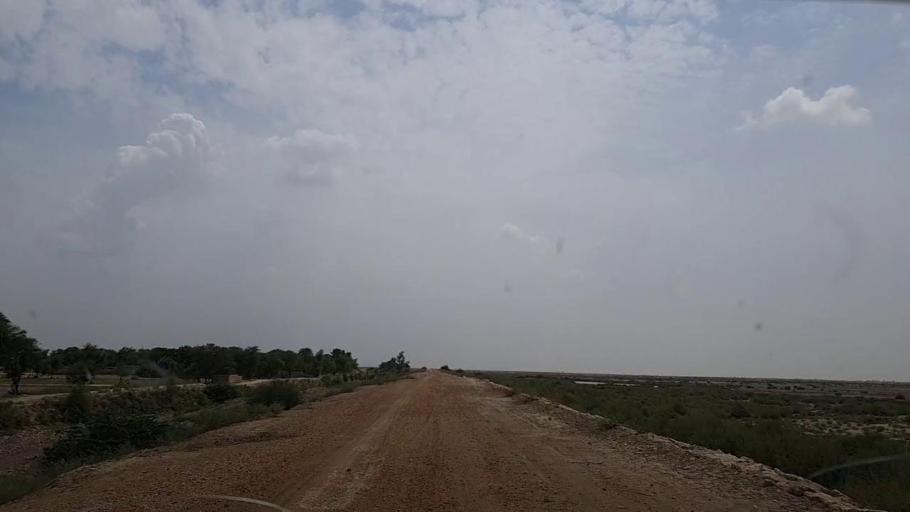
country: PK
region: Sindh
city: Phulji
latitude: 26.8089
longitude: 67.6062
